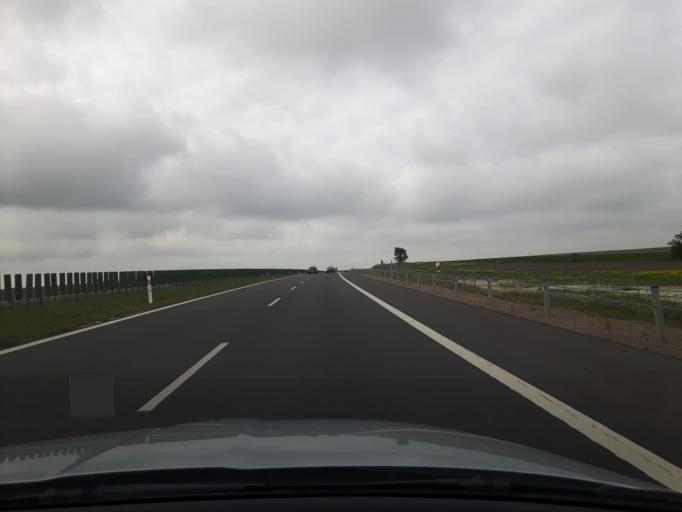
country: PL
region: Swietokrzyskie
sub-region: Powiat jedrzejowski
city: Sobkow
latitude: 50.6990
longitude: 20.3951
